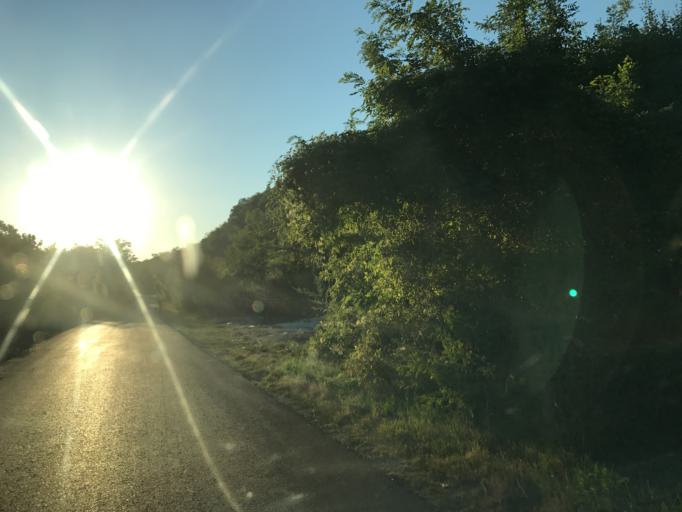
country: BG
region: Vidin
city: Bregovo
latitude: 44.1196
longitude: 22.5902
